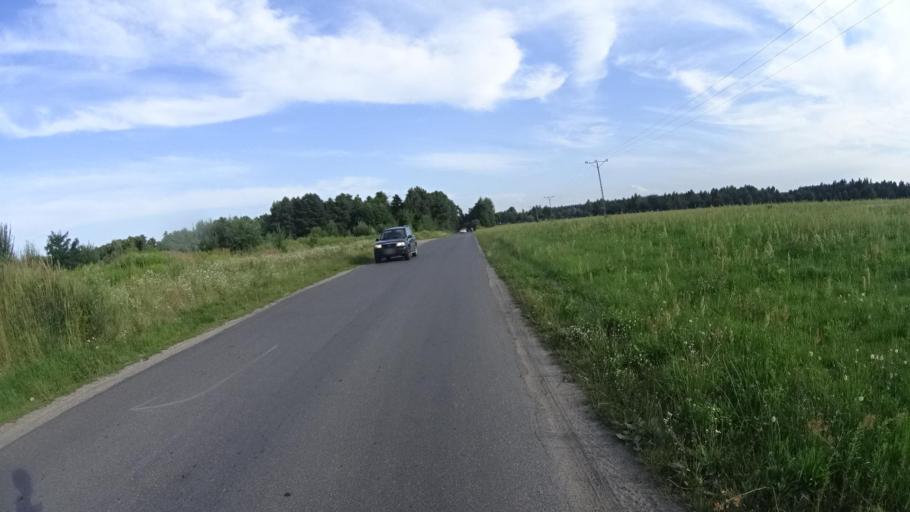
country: PL
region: Masovian Voivodeship
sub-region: Powiat piaseczynski
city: Tarczyn
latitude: 52.0138
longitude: 20.8009
